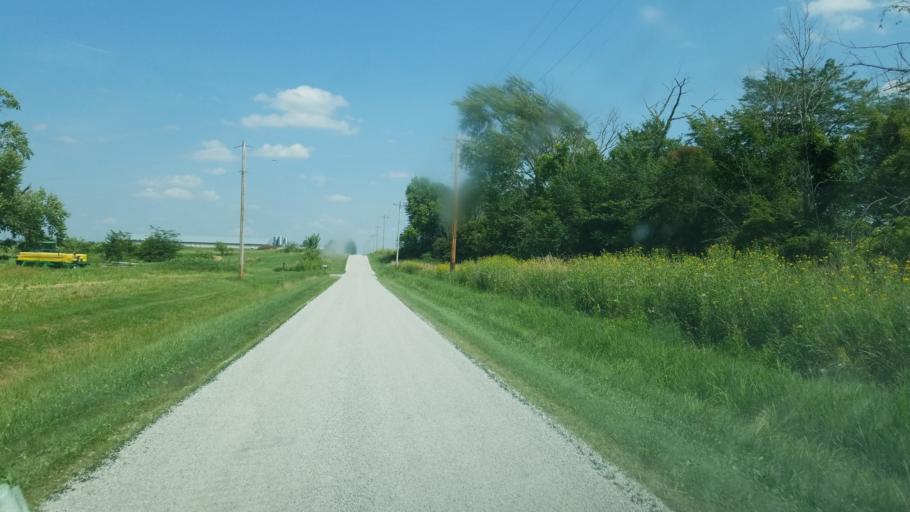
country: US
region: Ohio
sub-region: Sandusky County
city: Green Springs
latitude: 41.1389
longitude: -83.0426
